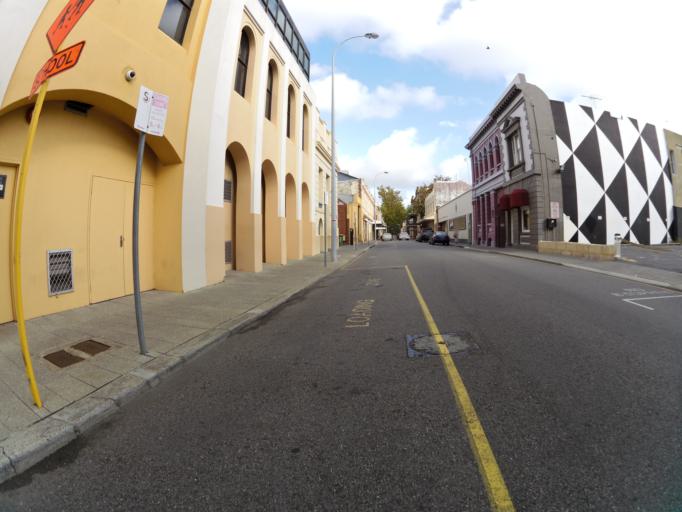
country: AU
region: Western Australia
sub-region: Fremantle
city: South Fremantle
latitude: -32.0545
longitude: 115.7438
